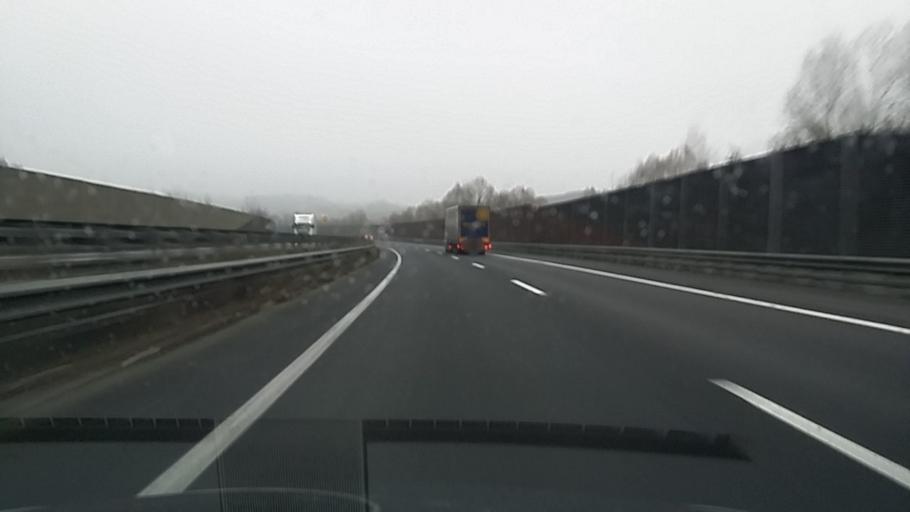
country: AT
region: Upper Austria
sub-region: Wels-Land
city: Offenhausen
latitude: 48.1769
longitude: 13.8360
